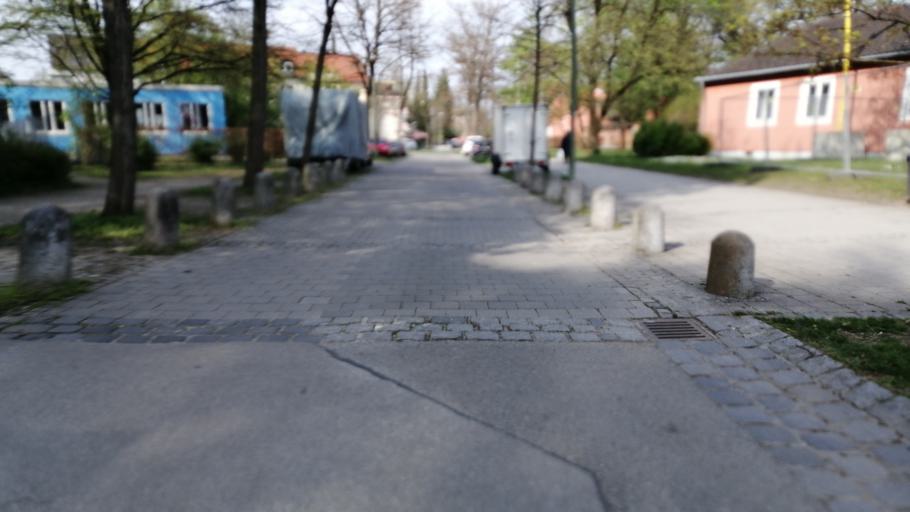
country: DE
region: Bavaria
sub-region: Upper Bavaria
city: Munich
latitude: 48.1796
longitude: 11.5800
